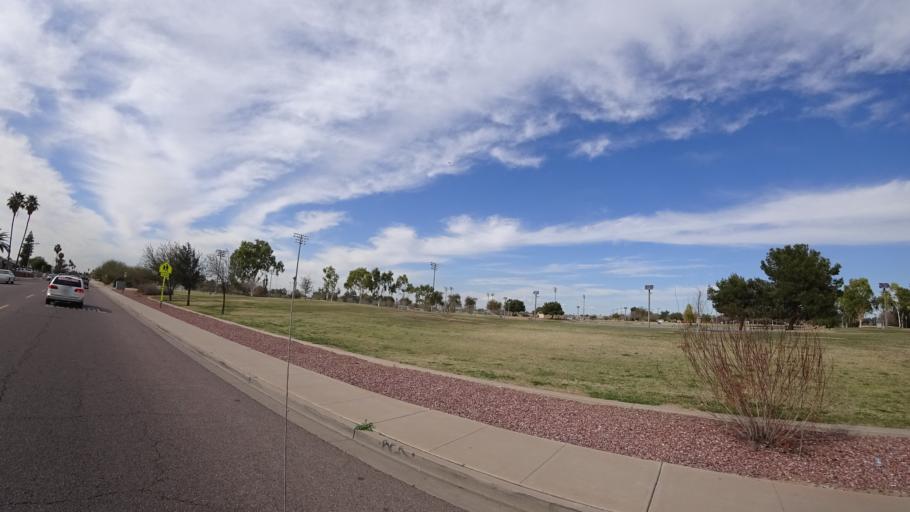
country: US
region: Arizona
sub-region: Maricopa County
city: Glendale
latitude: 33.4732
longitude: -112.1940
